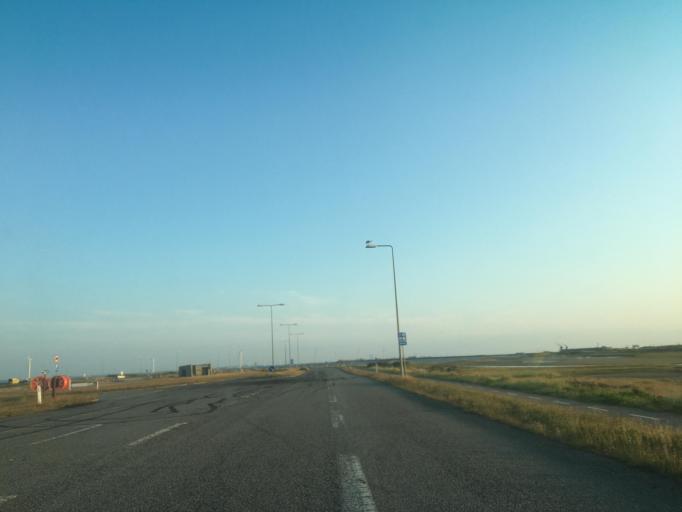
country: DK
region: Central Jutland
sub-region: Lemvig Kommune
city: Thyboron
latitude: 56.7046
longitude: 8.2461
